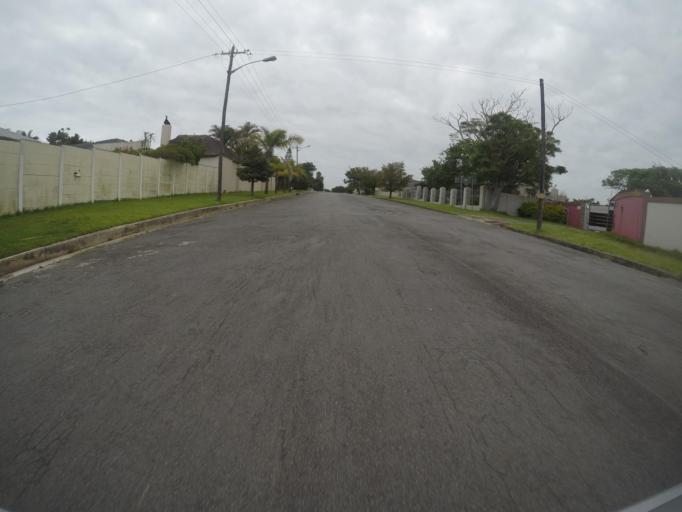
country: ZA
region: Eastern Cape
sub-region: Buffalo City Metropolitan Municipality
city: East London
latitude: -32.9905
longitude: 27.8983
